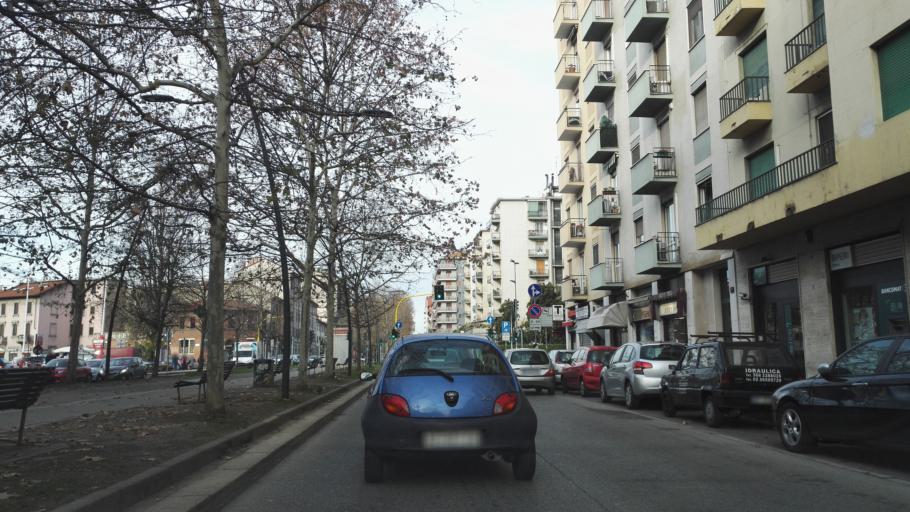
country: IT
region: Lombardy
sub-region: Citta metropolitana di Milano
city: Chiaravalle
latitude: 45.4421
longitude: 9.2201
